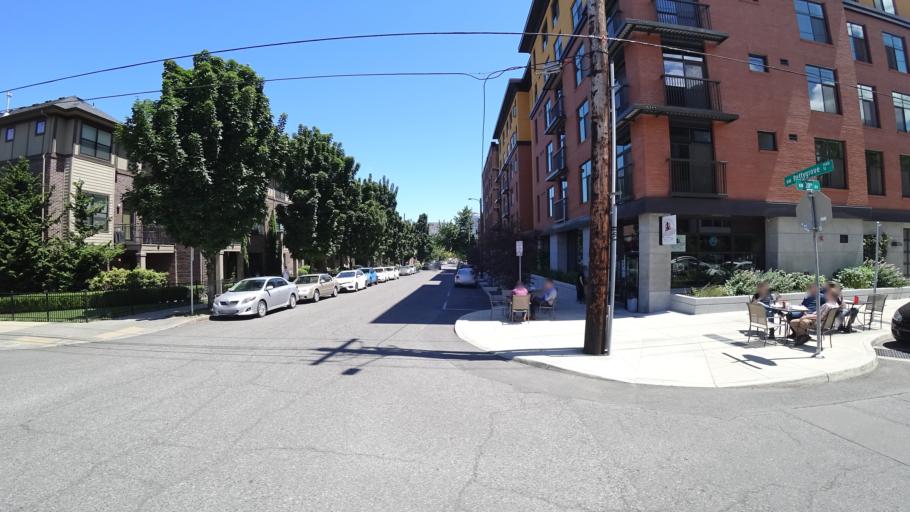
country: US
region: Oregon
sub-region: Multnomah County
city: Portland
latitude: 45.5327
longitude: -122.6927
